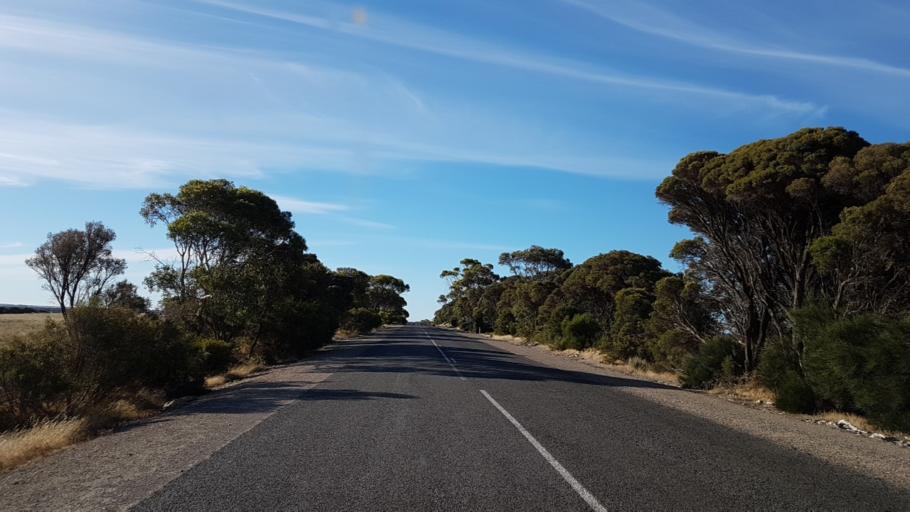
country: AU
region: South Australia
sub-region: Yorke Peninsula
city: Honiton
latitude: -34.9513
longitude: 137.0994
